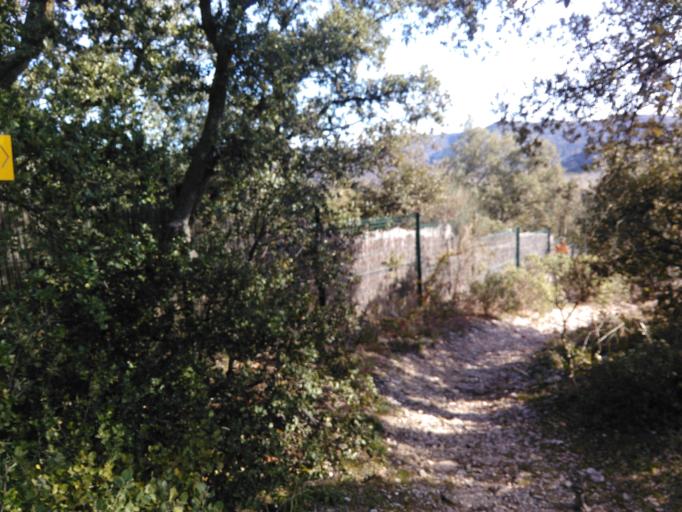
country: FR
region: Provence-Alpes-Cote d'Azur
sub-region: Departement du Vaucluse
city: Venasque
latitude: 43.9864
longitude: 5.1391
